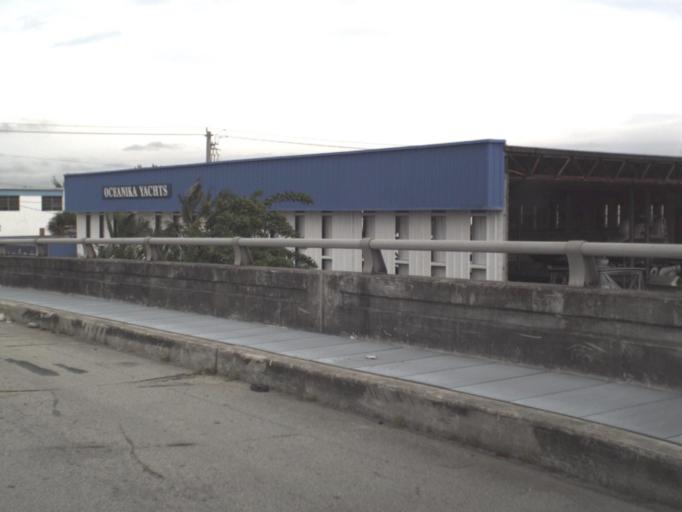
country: US
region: Florida
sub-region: Miami-Dade County
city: Brownsville
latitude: 25.7944
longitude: -80.2561
